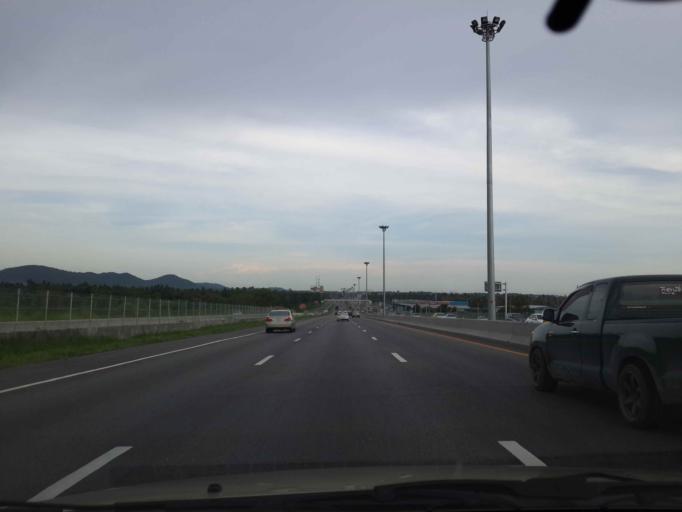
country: TH
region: Chon Buri
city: Ban Talat Bueng
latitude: 13.0296
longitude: 100.9964
